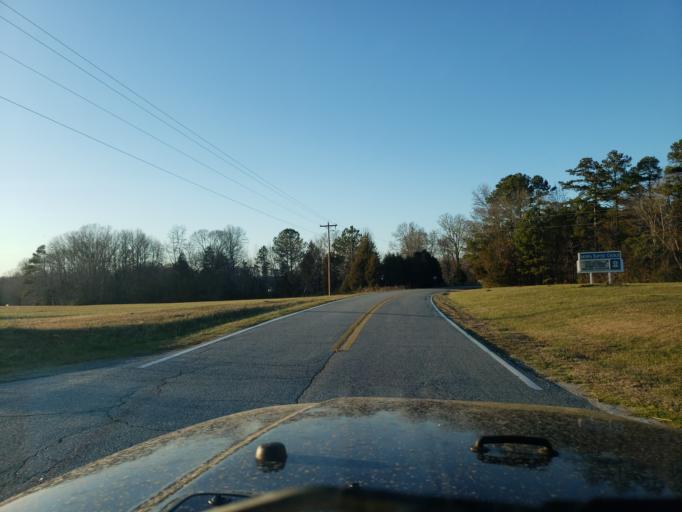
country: US
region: South Carolina
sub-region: Cherokee County
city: Blacksburg
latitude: 35.0518
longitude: -81.4230
